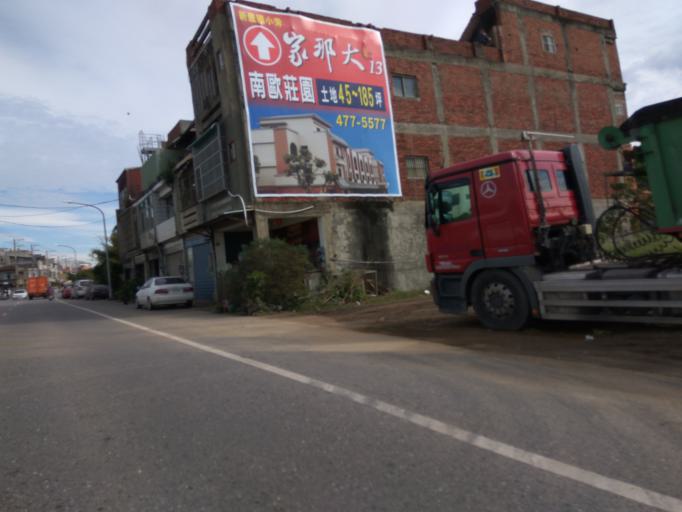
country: TW
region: Taiwan
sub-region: Hsinchu
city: Zhubei
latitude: 24.9675
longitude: 121.0992
